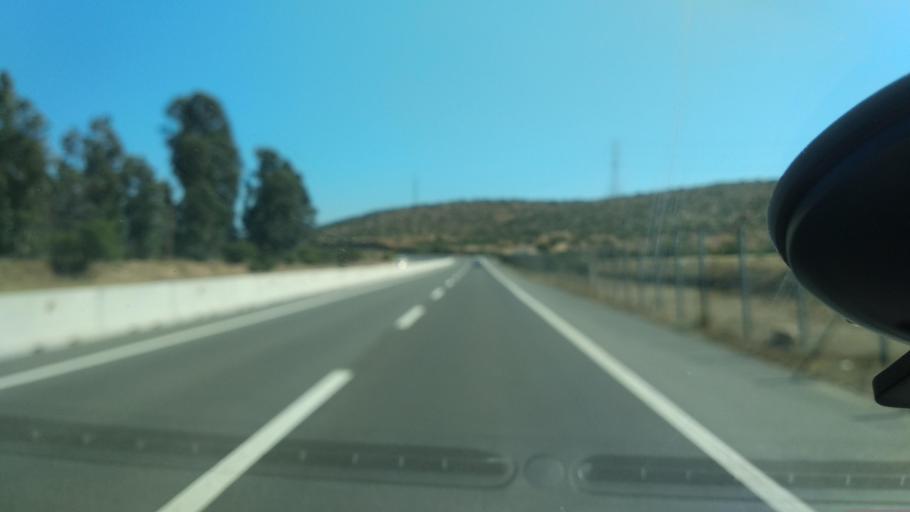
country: CL
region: Valparaiso
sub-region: Provincia de Marga Marga
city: Villa Alemana
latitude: -32.9928
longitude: -71.3288
